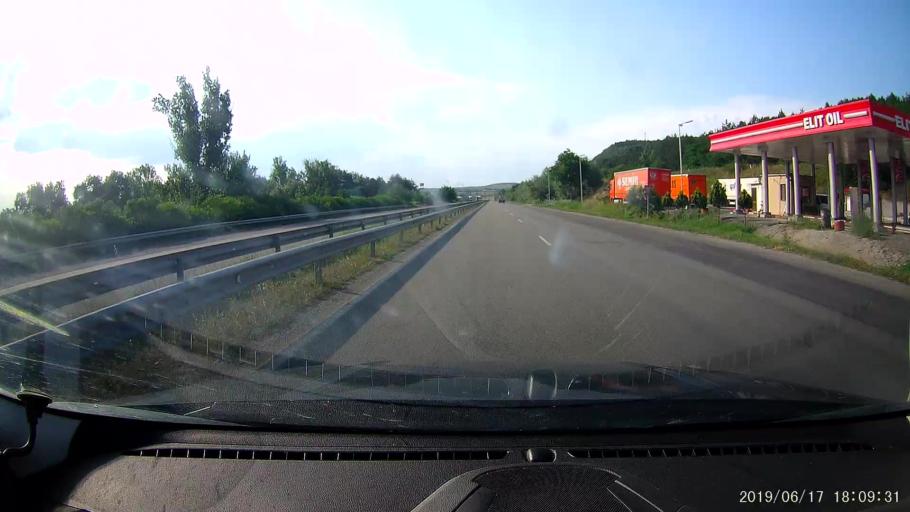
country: BG
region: Khaskovo
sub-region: Obshtina Lyubimets
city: Lyubimets
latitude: 41.8605
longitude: 26.0887
